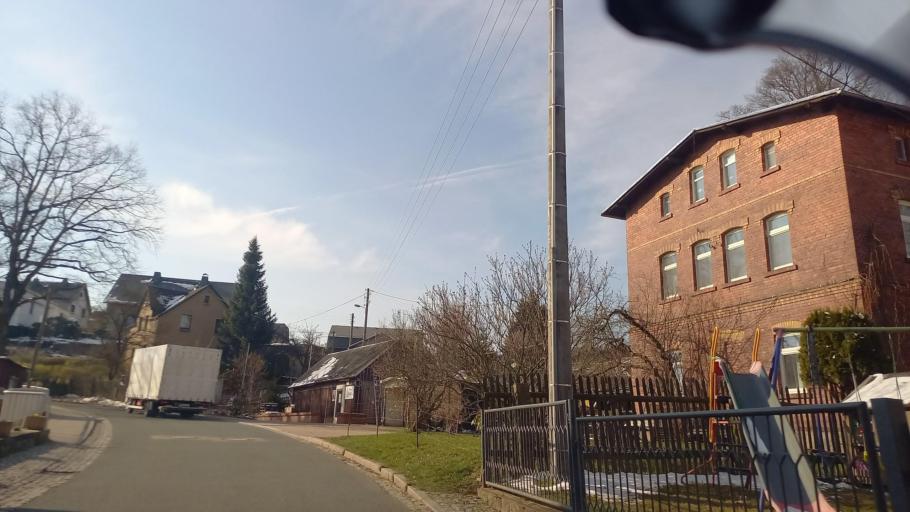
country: DE
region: Saxony
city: Stutzengrun
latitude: 50.5689
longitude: 12.4812
